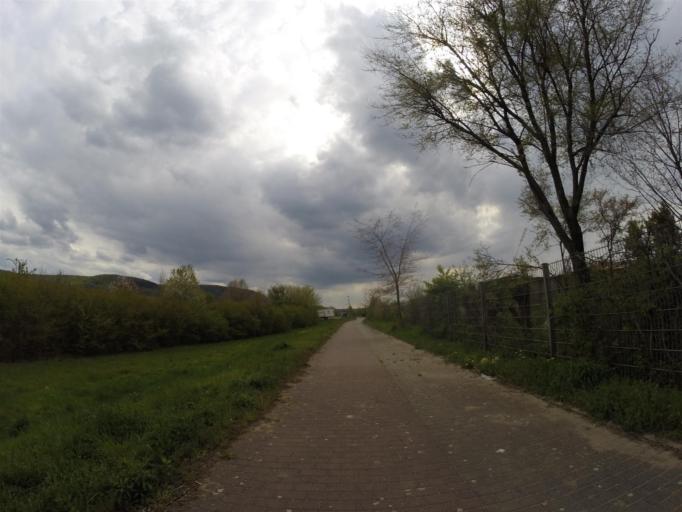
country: DE
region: Thuringia
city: Neuengonna
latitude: 50.9593
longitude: 11.6274
